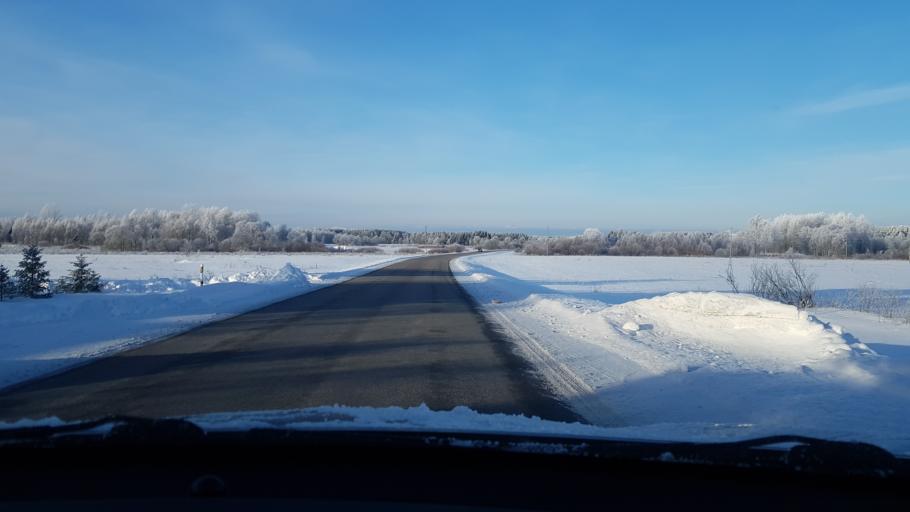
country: EE
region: Harju
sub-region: Harku vald
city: Tabasalu
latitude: 59.3684
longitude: 24.4794
